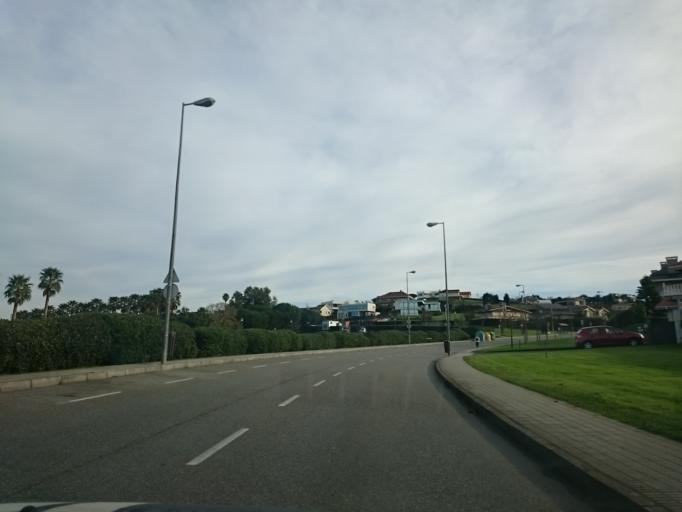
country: ES
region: Asturias
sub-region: Province of Asturias
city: Gijon
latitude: 43.5335
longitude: -5.6000
